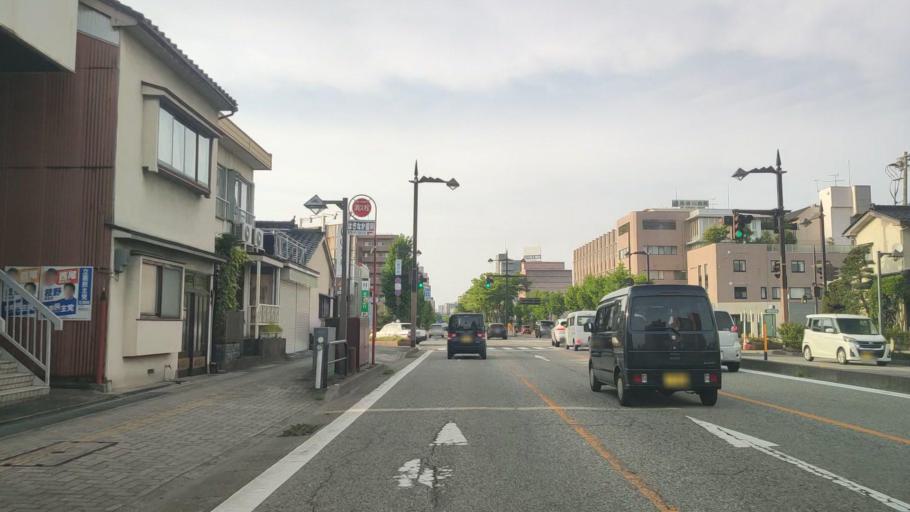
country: JP
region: Toyama
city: Toyama-shi
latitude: 36.6830
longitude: 137.2116
